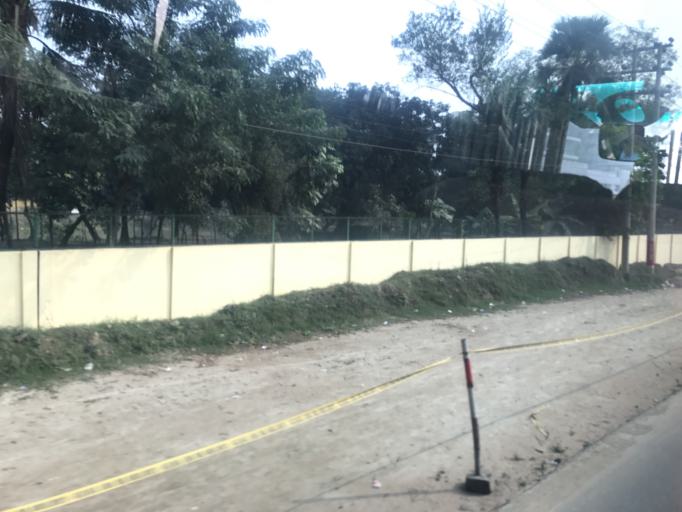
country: BD
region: Dhaka
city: Tungi
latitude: 23.9012
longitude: 90.2691
